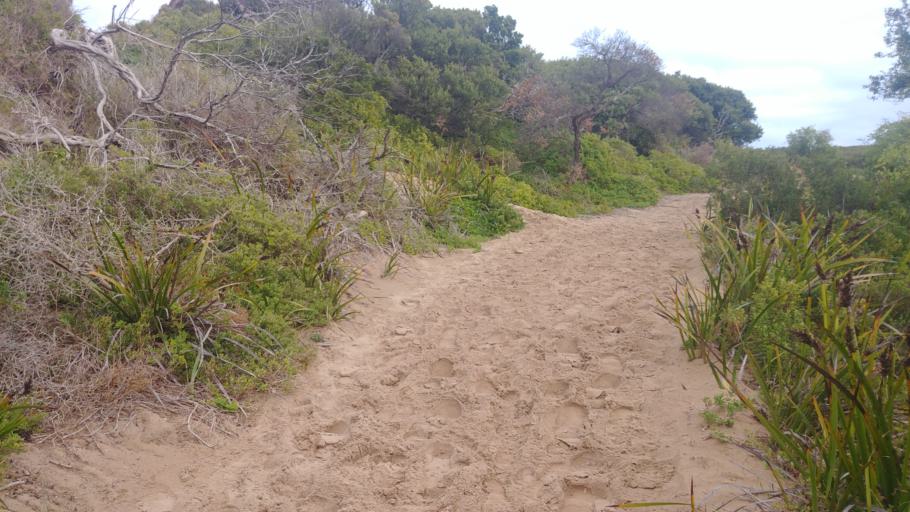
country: AU
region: Victoria
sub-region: Mornington Peninsula
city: Blairgowrie
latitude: -38.3922
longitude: 144.7925
